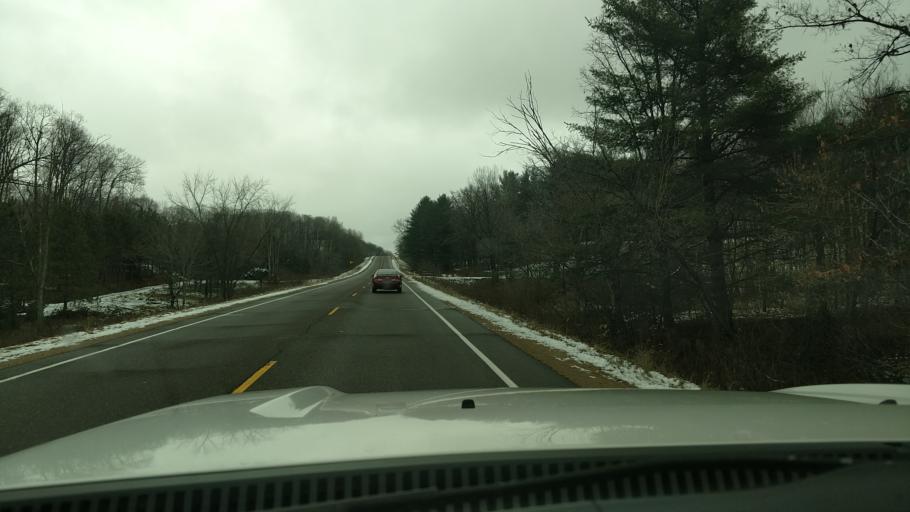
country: US
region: Wisconsin
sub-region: Dunn County
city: Boyceville
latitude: 45.1334
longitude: -91.9905
